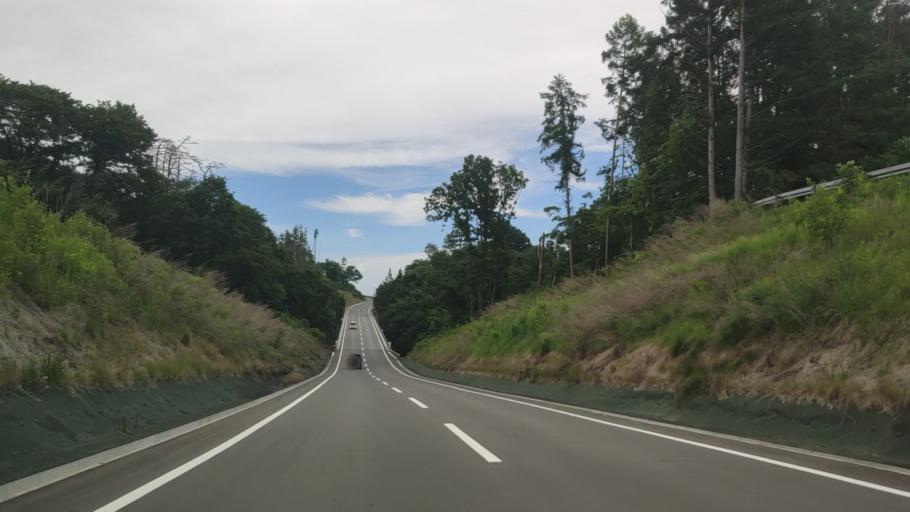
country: JP
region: Nagano
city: Kamimaruko
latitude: 36.2766
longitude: 138.2947
